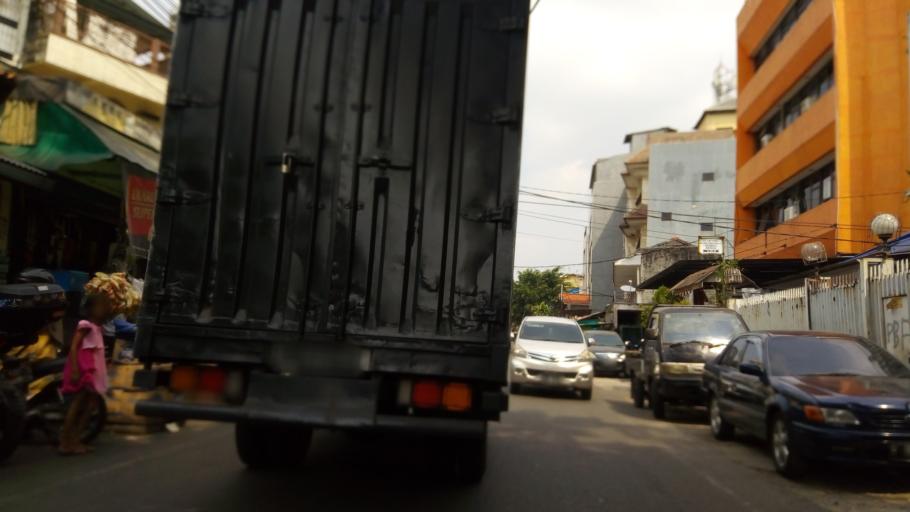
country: ID
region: Jakarta Raya
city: Jakarta
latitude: -6.1565
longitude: 106.8313
